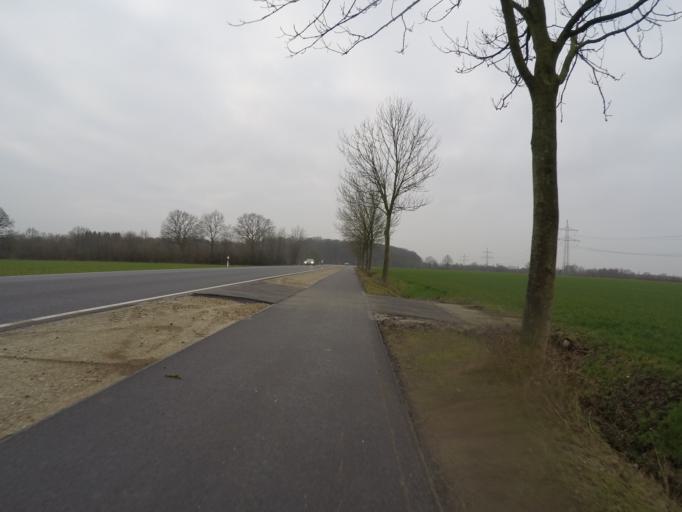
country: DE
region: Schleswig-Holstein
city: Borstel-Hohenraden
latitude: 53.7110
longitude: 9.8450
